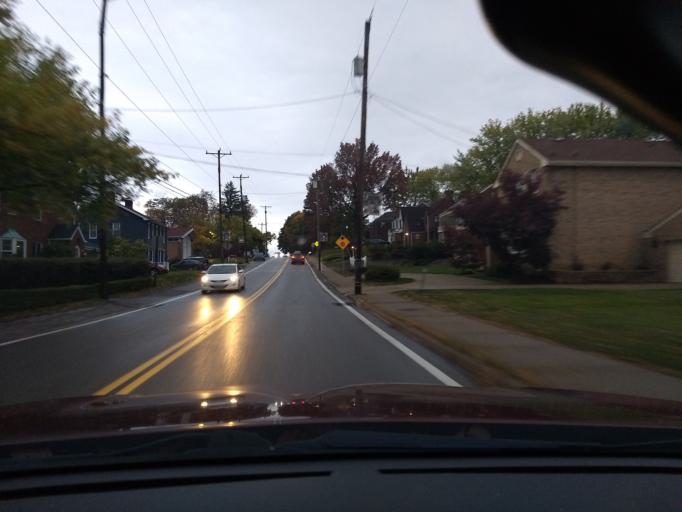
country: US
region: Pennsylvania
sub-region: Allegheny County
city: Pleasant Hills
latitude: 40.3299
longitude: -79.9593
